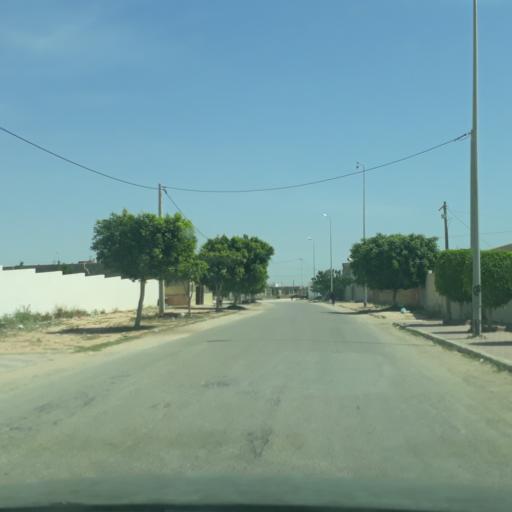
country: TN
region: Safaqis
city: Al Qarmadah
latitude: 34.8255
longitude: 10.7828
